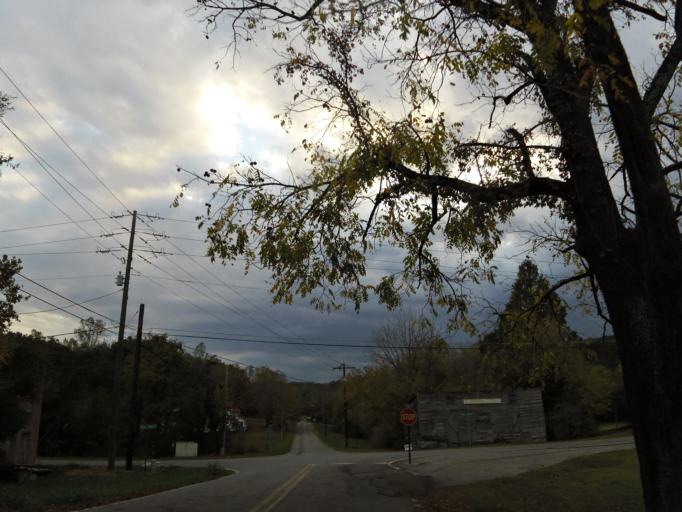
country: US
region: Tennessee
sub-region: Blount County
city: Louisville
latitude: 35.7785
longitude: -84.0907
